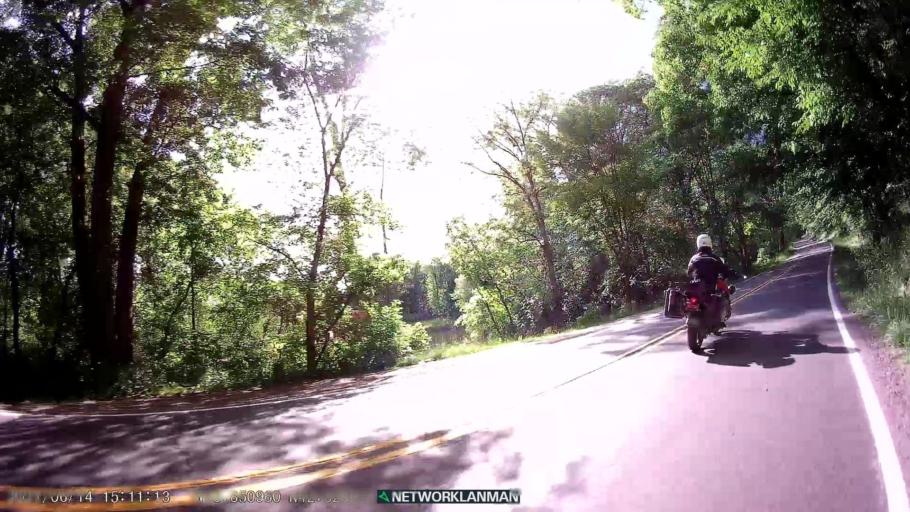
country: US
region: Michigan
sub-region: Washtenaw County
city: Dexter
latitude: 42.3267
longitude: -83.8515
